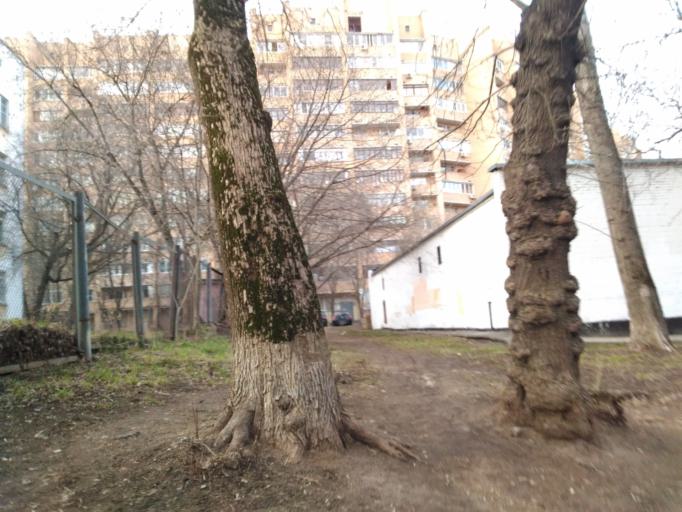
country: RU
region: Moskovskaya
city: Khoroshevo-Mnevniki
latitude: 55.7857
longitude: 37.4608
